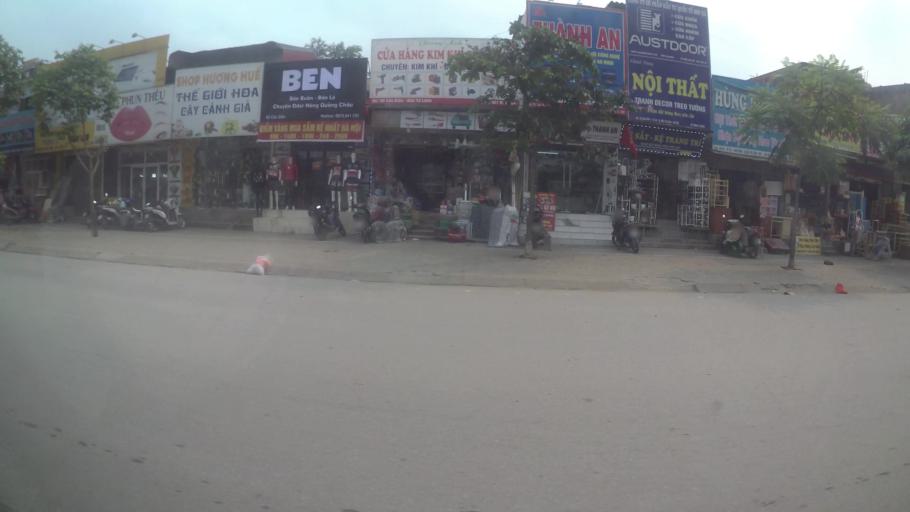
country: VN
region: Ha Noi
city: Cau Dien
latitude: 21.0428
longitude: 105.7578
